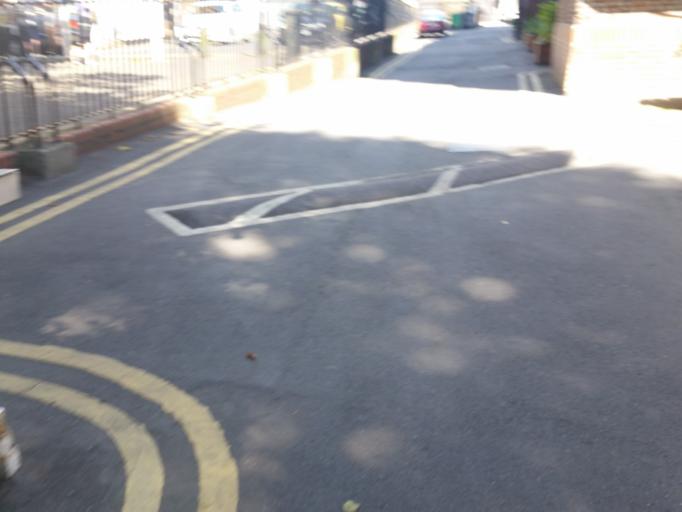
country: GB
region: England
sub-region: Greater London
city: Bethnal Green
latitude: 51.5388
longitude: -0.0595
